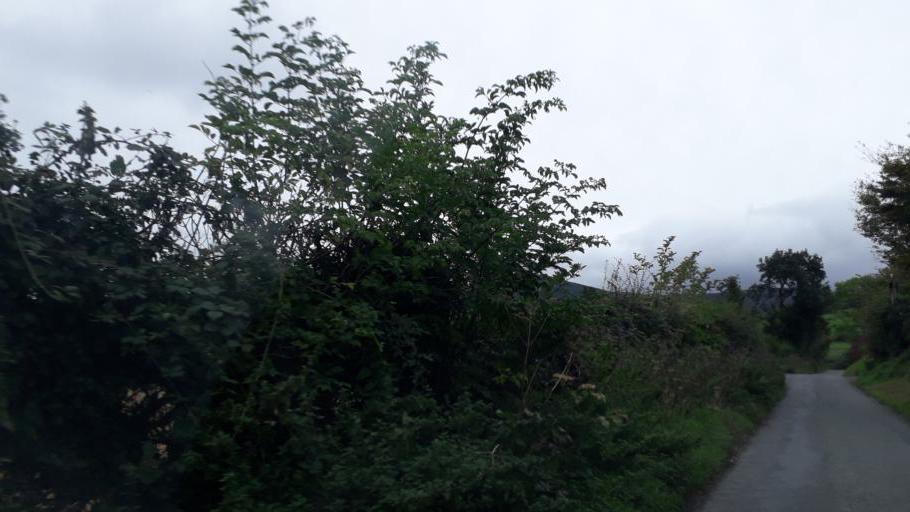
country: IE
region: Leinster
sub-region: Wicklow
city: Enniskerry
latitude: 53.1844
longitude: -6.2050
